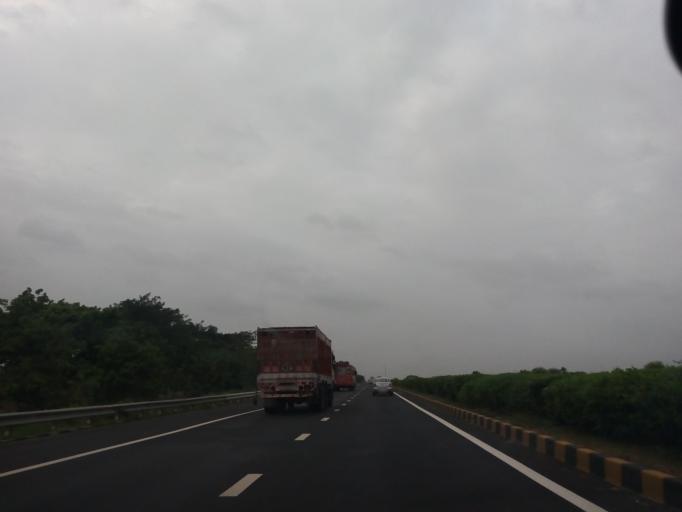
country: IN
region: Gujarat
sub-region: Kheda
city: Nadiad
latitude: 22.7449
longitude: 72.8623
